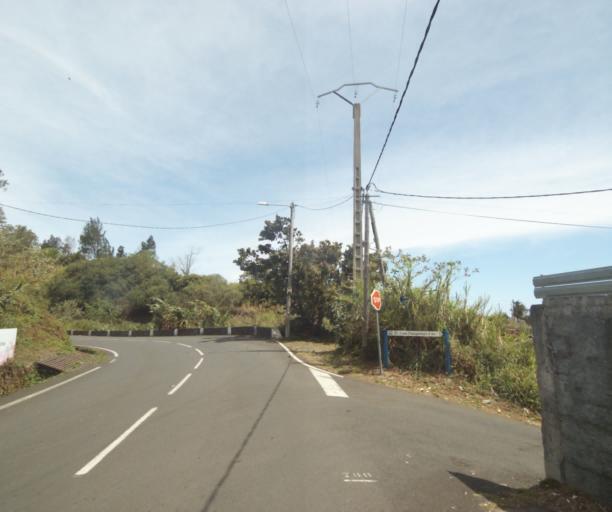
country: RE
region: Reunion
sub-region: Reunion
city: Trois-Bassins
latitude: -21.0617
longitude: 55.3080
